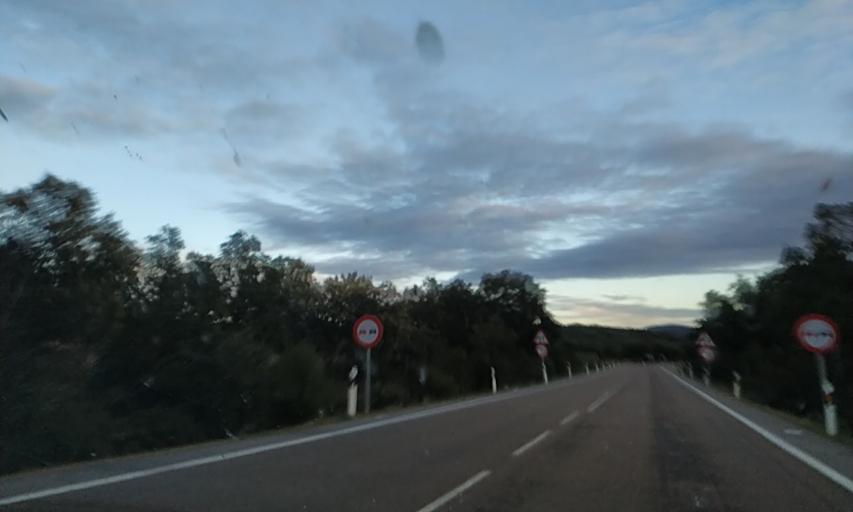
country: ES
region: Extremadura
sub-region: Provincia de Badajoz
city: Puebla de Obando
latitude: 39.2787
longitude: -6.5207
